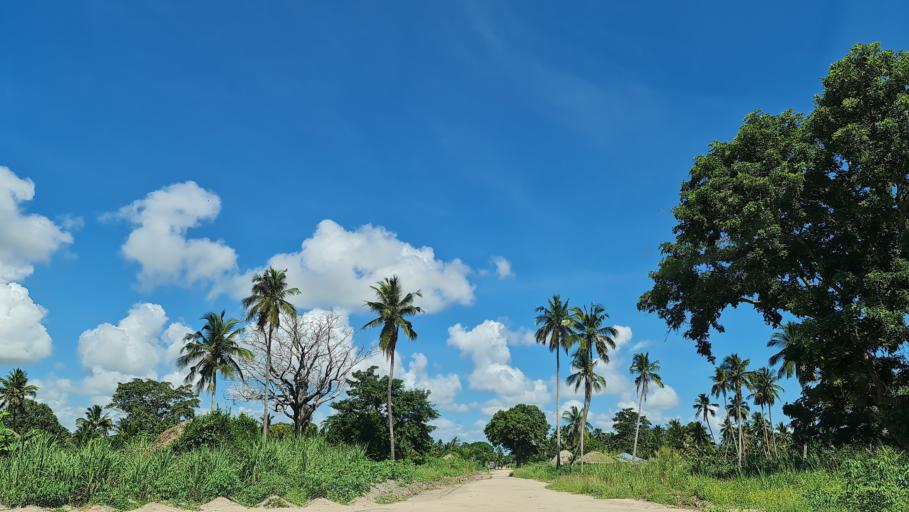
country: MZ
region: Zambezia
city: Quelimane
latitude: -17.3824
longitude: 37.5150
